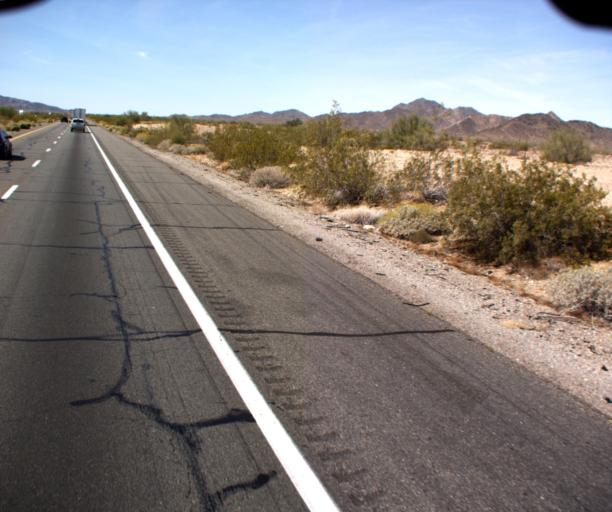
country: US
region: Arizona
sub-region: La Paz County
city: Quartzsite
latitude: 33.6554
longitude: -114.2725
